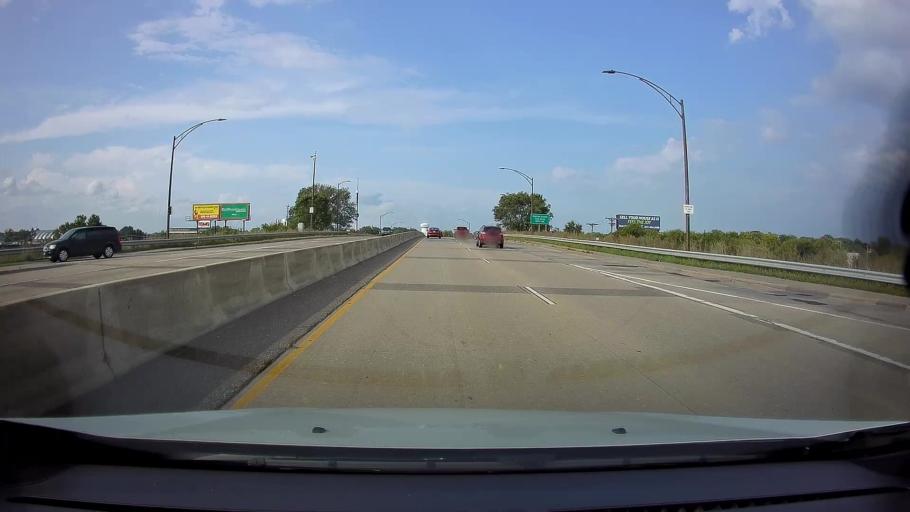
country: US
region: Minnesota
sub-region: Ramsey County
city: Falcon Heights
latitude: 44.9723
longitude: -93.1670
